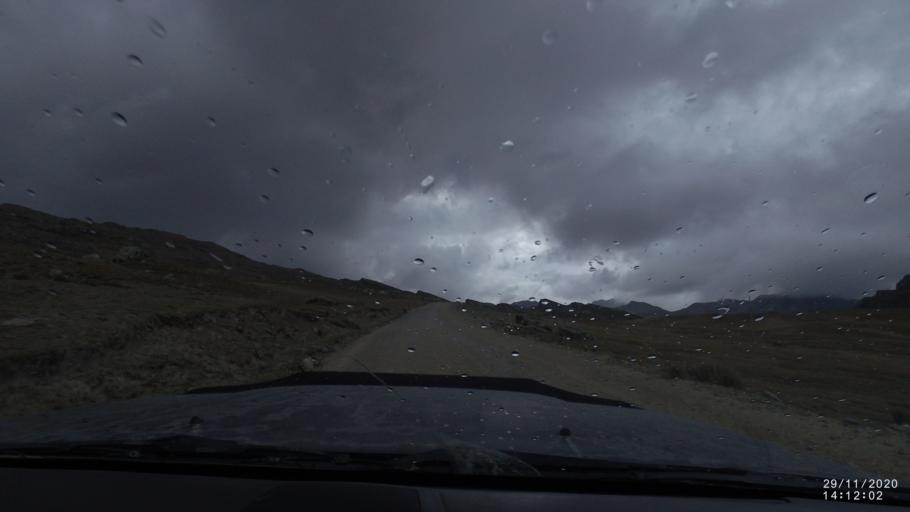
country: BO
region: Cochabamba
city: Sipe Sipe
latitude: -17.2367
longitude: -66.3914
